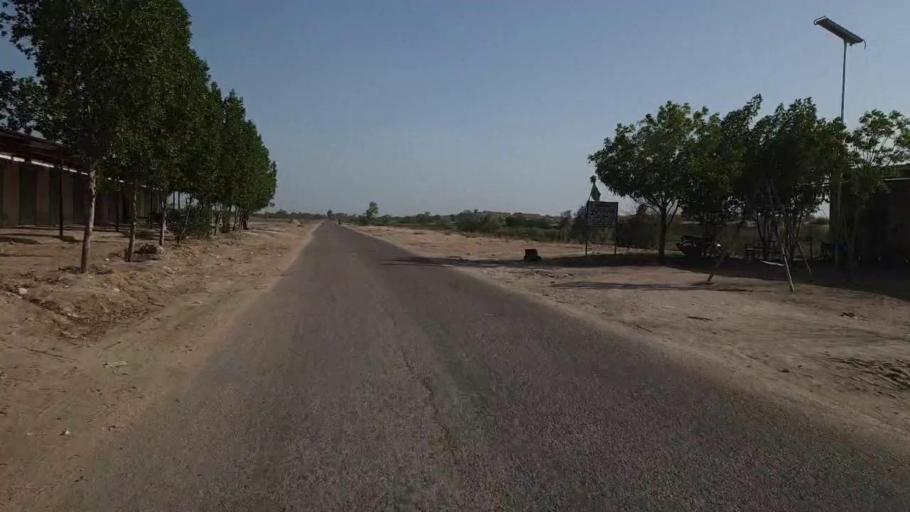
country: PK
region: Sindh
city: Daur
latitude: 26.4732
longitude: 68.4540
